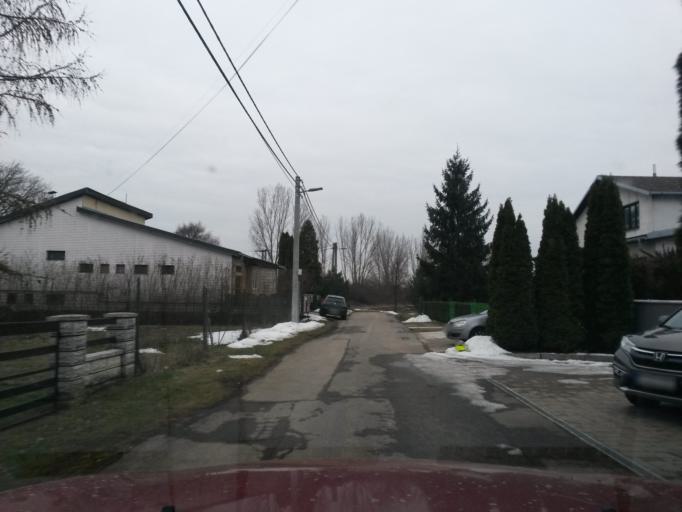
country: SK
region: Kosicky
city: Michalovce
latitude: 48.7262
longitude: 21.8636
